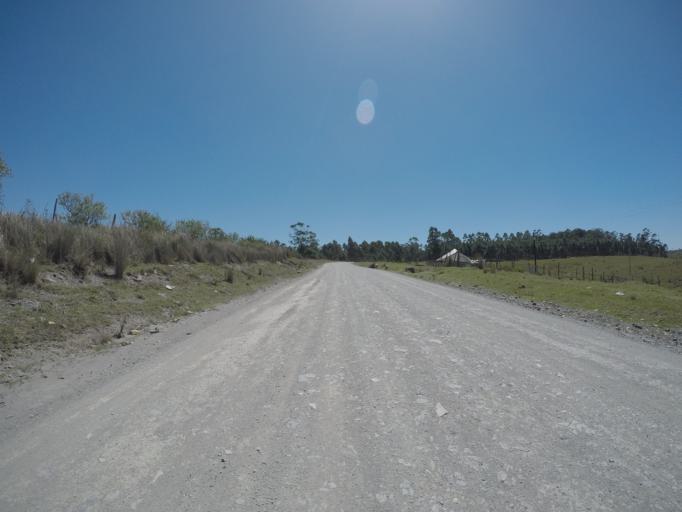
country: ZA
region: Eastern Cape
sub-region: OR Tambo District Municipality
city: Libode
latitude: -31.9629
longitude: 29.0248
